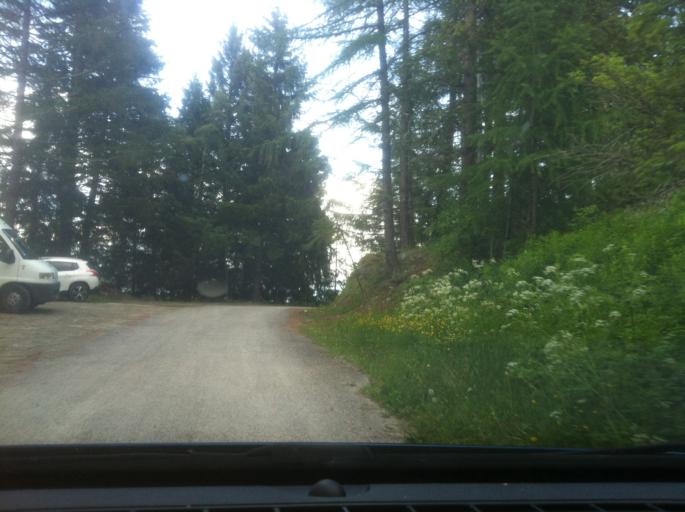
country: IT
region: Aosta Valley
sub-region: Valle d'Aosta
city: Nus
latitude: 45.7069
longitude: 7.4721
